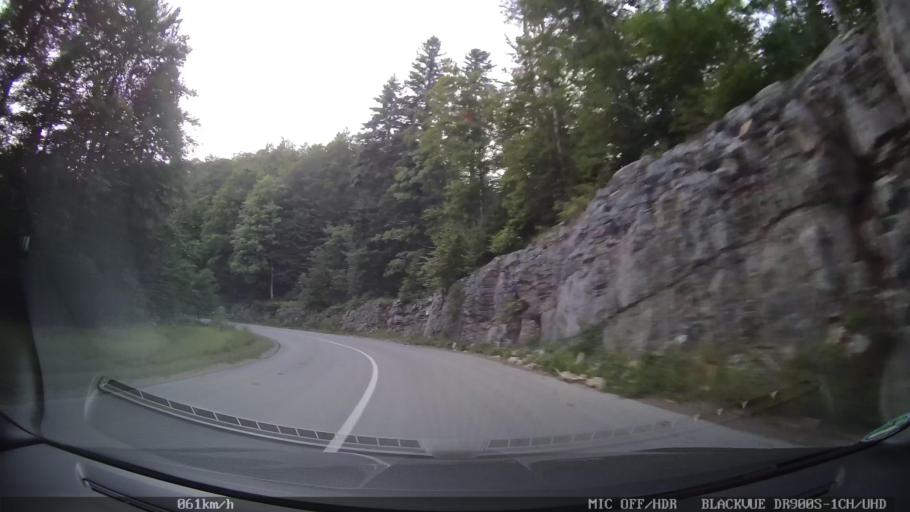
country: HR
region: Primorsko-Goranska
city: Novi Vinodolski
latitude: 45.1776
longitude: 14.9822
